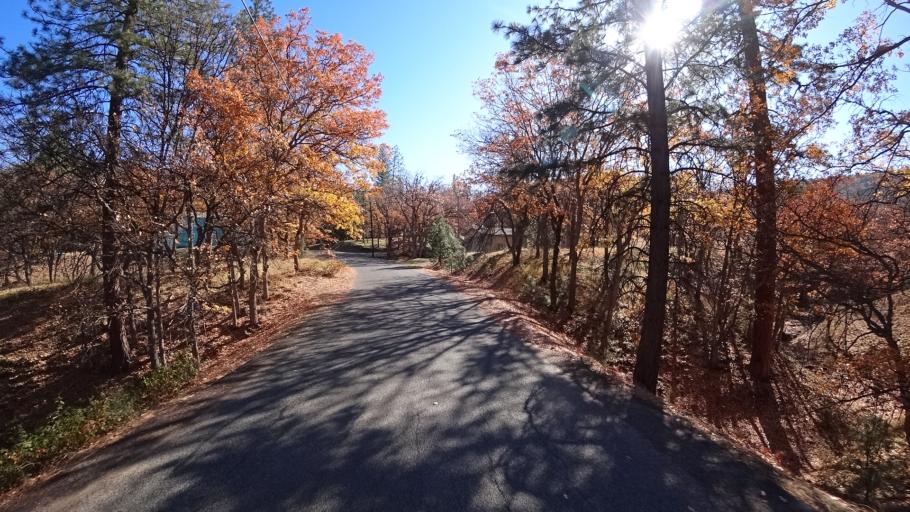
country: US
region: California
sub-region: Siskiyou County
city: Montague
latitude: 41.9741
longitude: -122.3213
